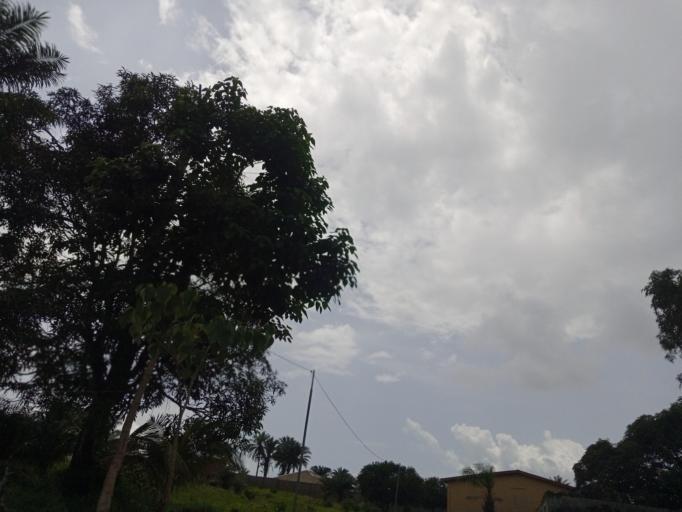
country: SL
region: Northern Province
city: Sawkta
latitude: 8.6349
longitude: -13.2014
